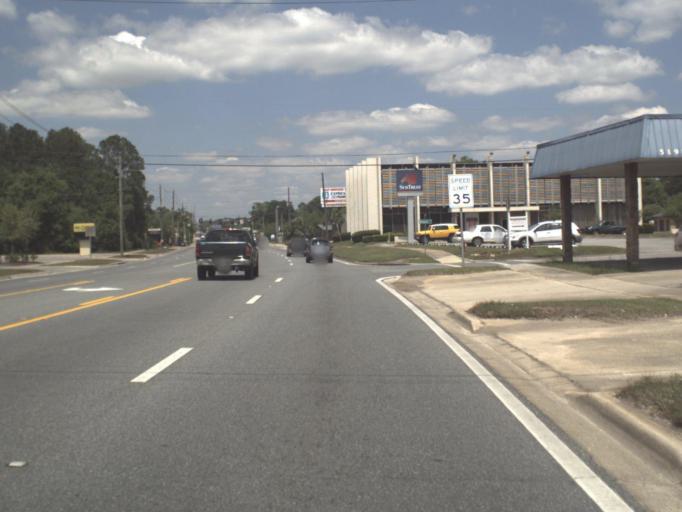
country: US
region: Florida
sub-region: Santa Rosa County
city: Milton
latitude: 30.6231
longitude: -87.0432
